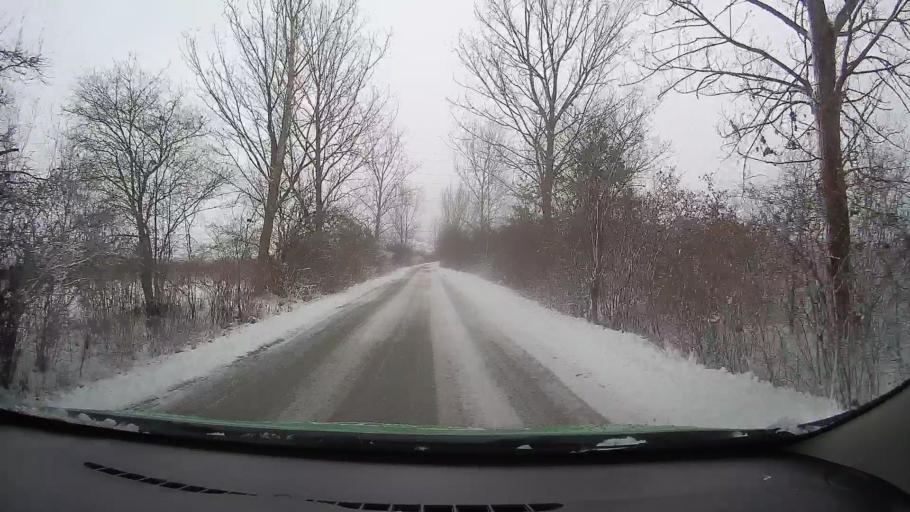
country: RO
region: Hunedoara
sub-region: Municipiul Hunedoara
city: Pestisu Mare
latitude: 45.8077
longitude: 22.9127
